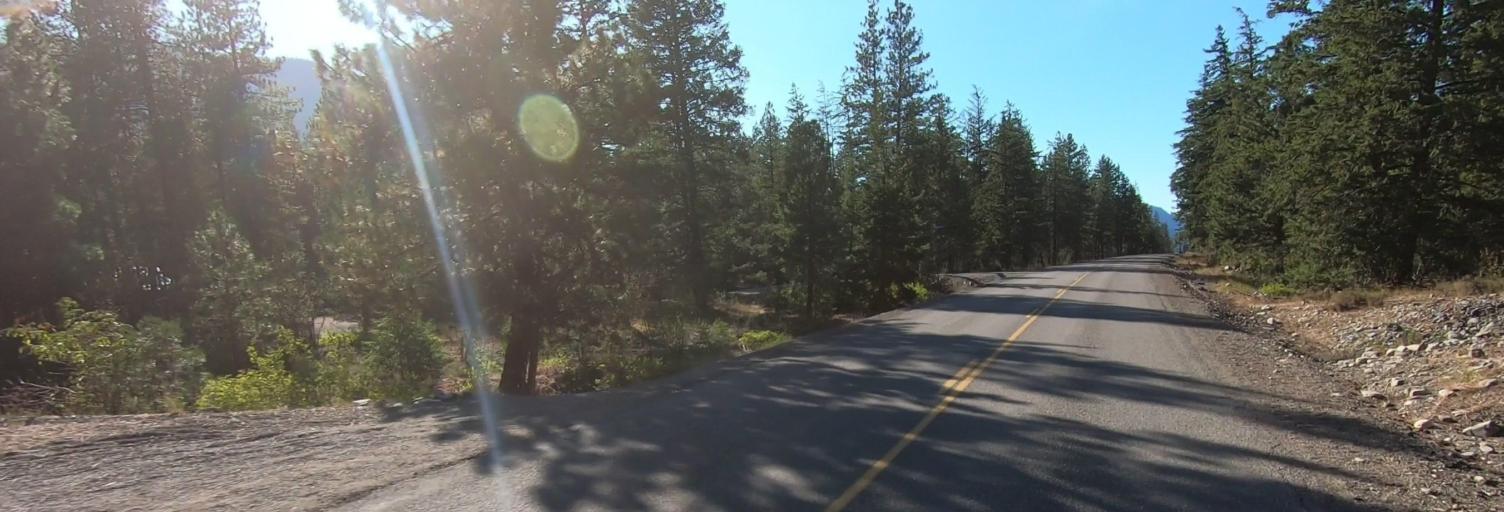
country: US
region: Washington
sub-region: Chelan County
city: Granite Falls
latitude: 48.5800
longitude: -120.3764
